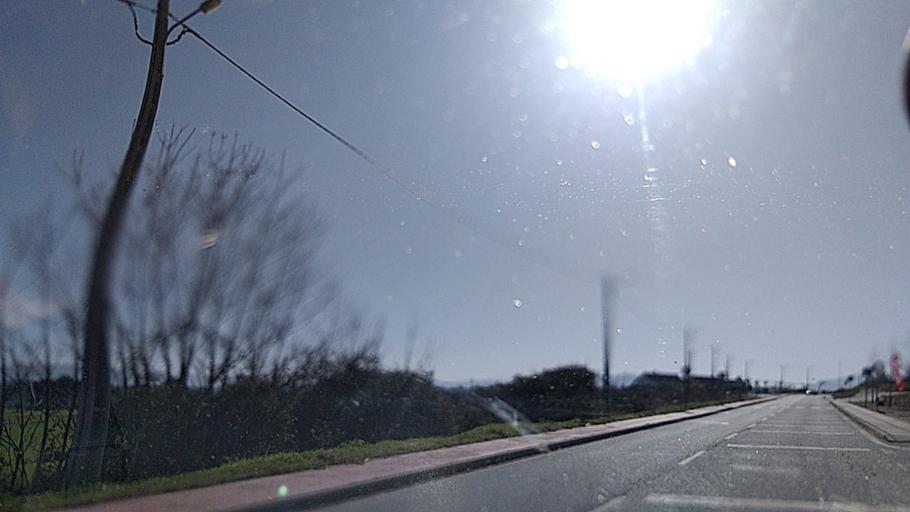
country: PT
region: Guarda
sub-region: Celorico da Beira
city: Celorico da Beira
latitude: 40.6520
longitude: -7.3835
